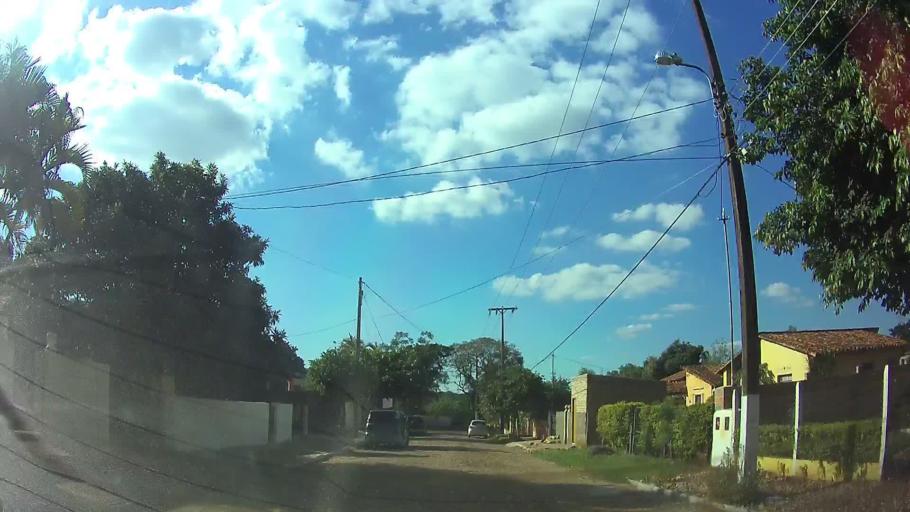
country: PY
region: Central
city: San Lorenzo
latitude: -25.2746
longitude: -57.4639
